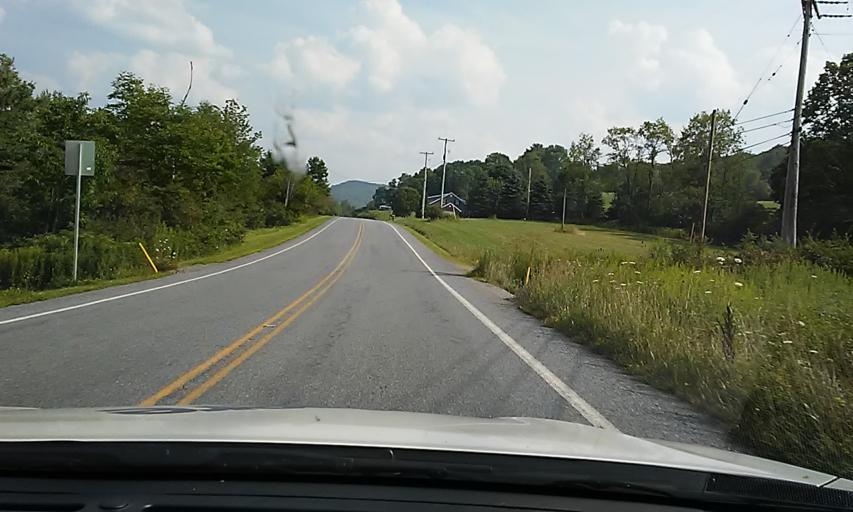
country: US
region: New York
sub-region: Allegany County
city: Wellsville
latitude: 41.9841
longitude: -77.8669
